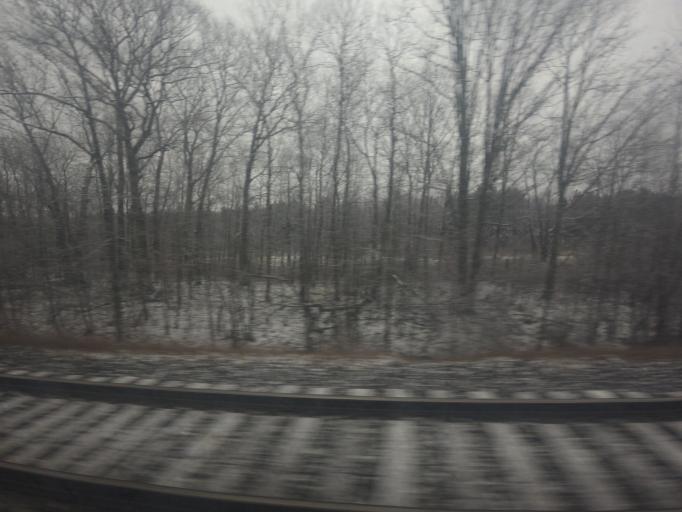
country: US
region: New York
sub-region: Jefferson County
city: Alexandria Bay
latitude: 44.4333
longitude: -75.9688
